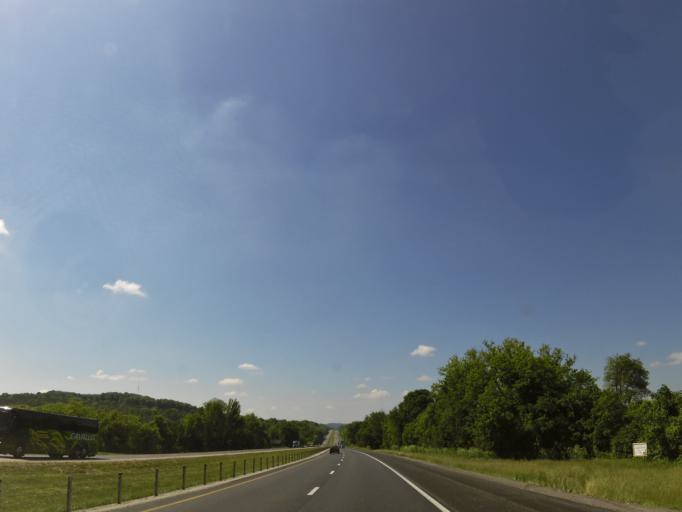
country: US
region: Kentucky
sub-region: Rockcastle County
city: Brodhead
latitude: 37.4274
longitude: -84.3437
